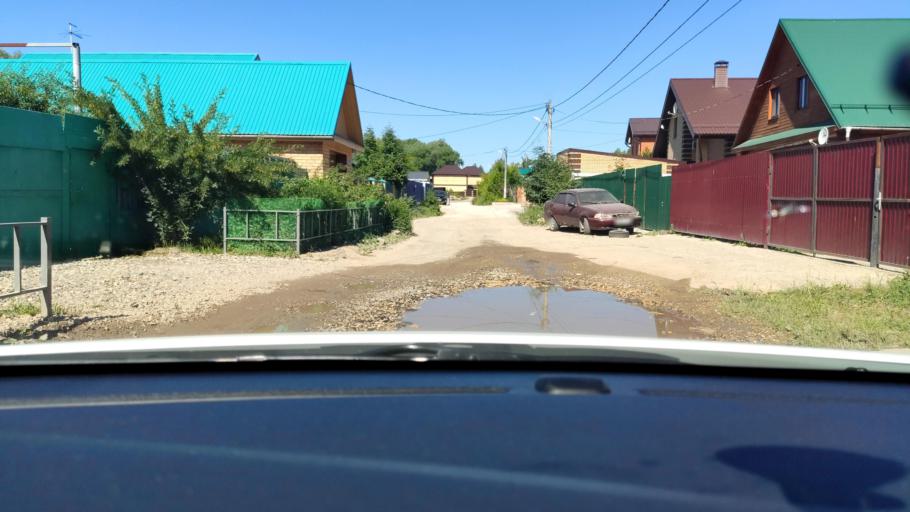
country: RU
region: Tatarstan
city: Stolbishchi
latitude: 55.7479
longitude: 49.2837
